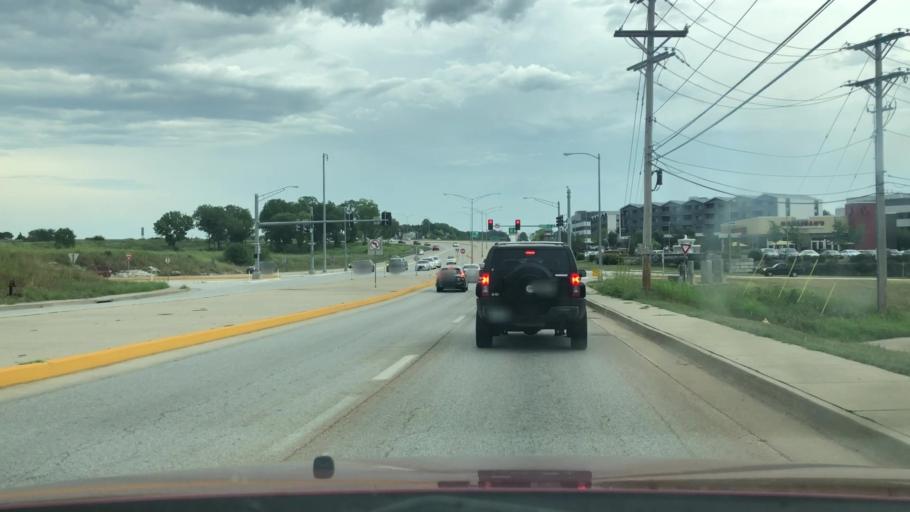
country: US
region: Missouri
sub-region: Greene County
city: Springfield
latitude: 37.1371
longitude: -93.2579
